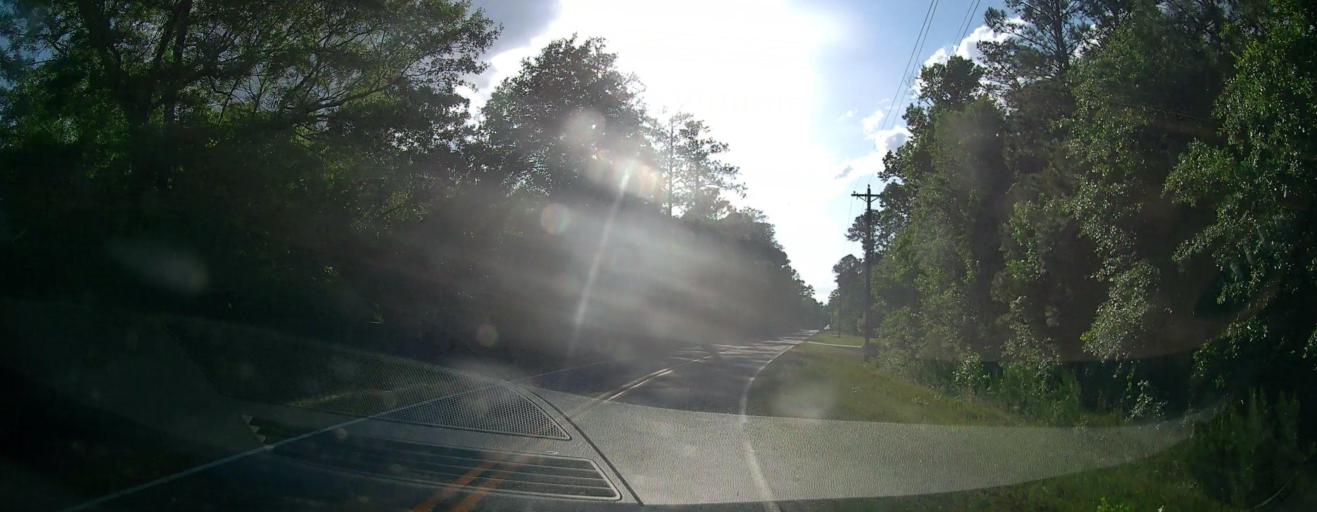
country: US
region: Georgia
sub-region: Peach County
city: Byron
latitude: 32.6712
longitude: -83.7919
